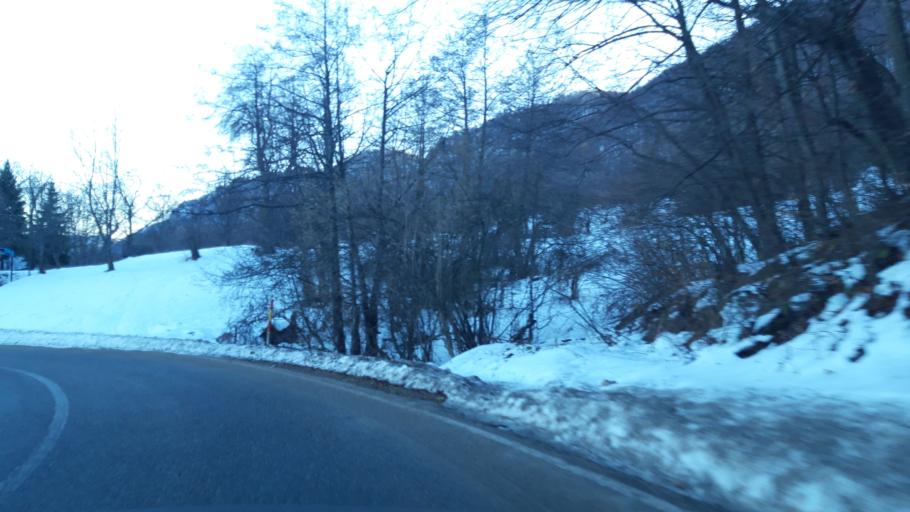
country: BA
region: Republika Srpska
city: Vlasenica
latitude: 44.1601
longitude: 18.9451
